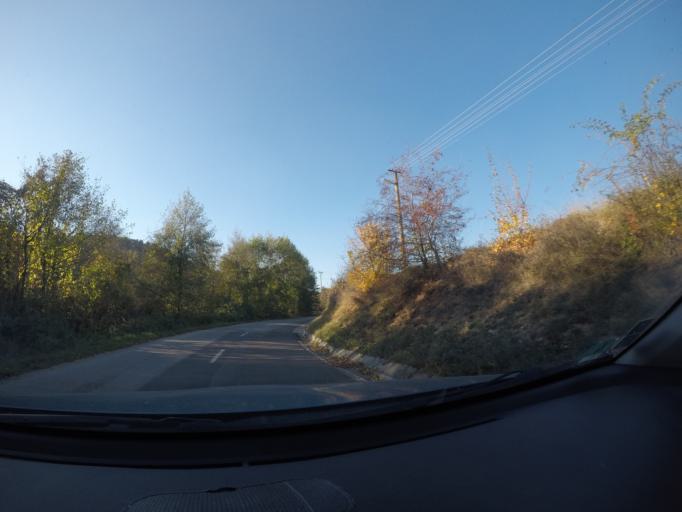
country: SK
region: Nitriansky
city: Nemsova
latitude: 48.9673
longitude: 18.0978
